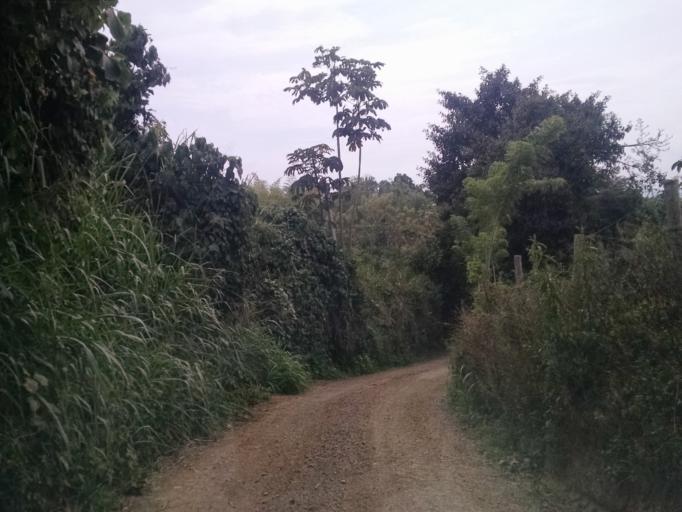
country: CO
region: Valle del Cauca
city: Ulloa
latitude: 4.7195
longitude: -75.7376
